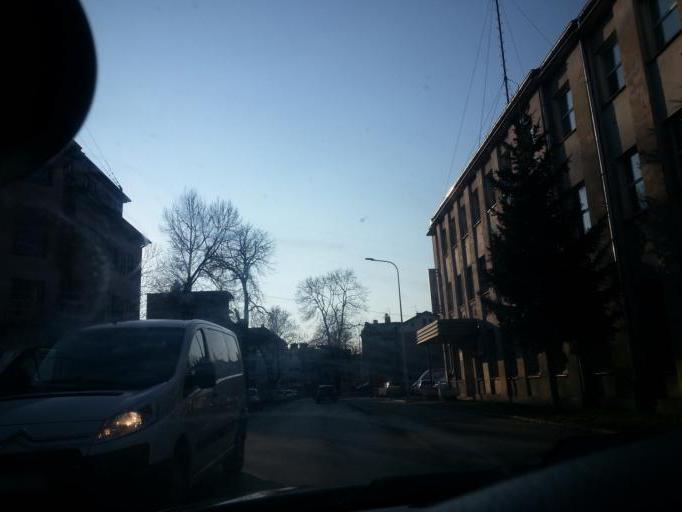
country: PL
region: Lower Silesian Voivodeship
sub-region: Jelenia Gora
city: Jelenia Gora
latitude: 50.9020
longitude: 15.7400
